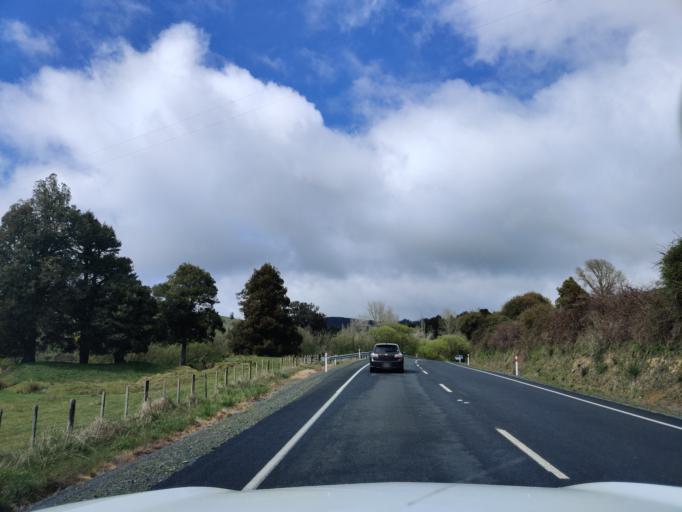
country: NZ
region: Waikato
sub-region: Otorohanga District
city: Otorohanga
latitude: -38.6032
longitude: 175.2156
